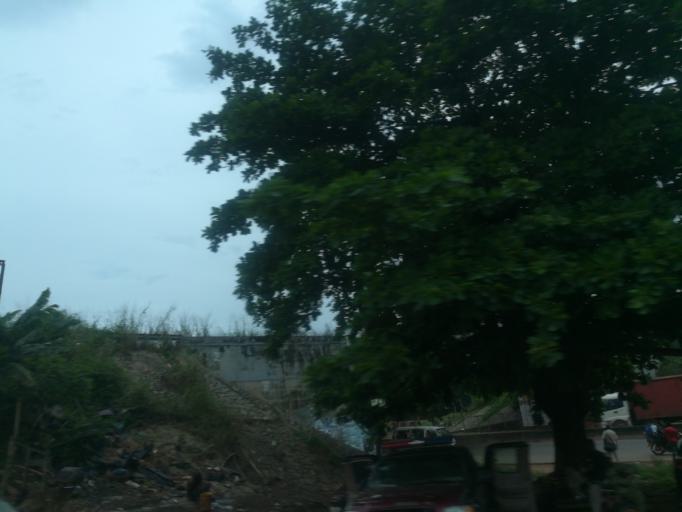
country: NG
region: Oyo
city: Ibadan
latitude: 7.3924
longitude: 3.9727
